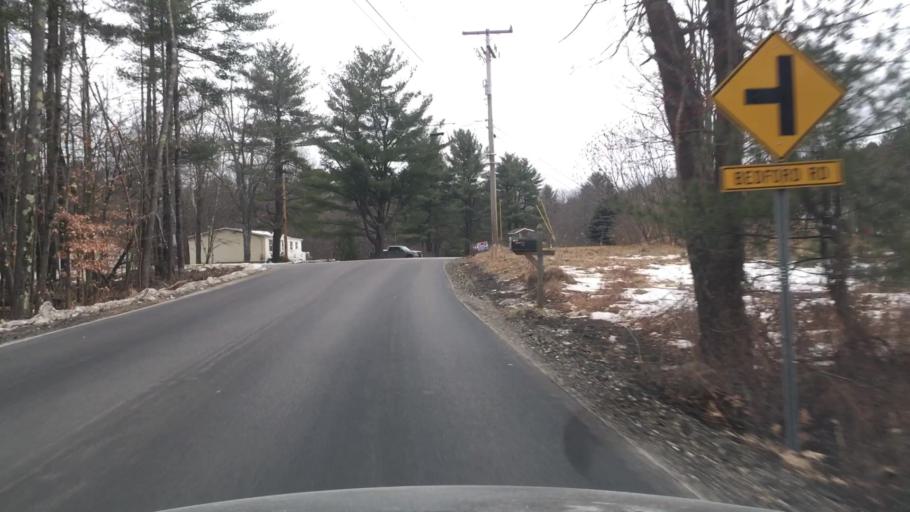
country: US
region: New Hampshire
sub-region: Hillsborough County
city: Goffstown
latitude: 42.9707
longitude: -71.6215
